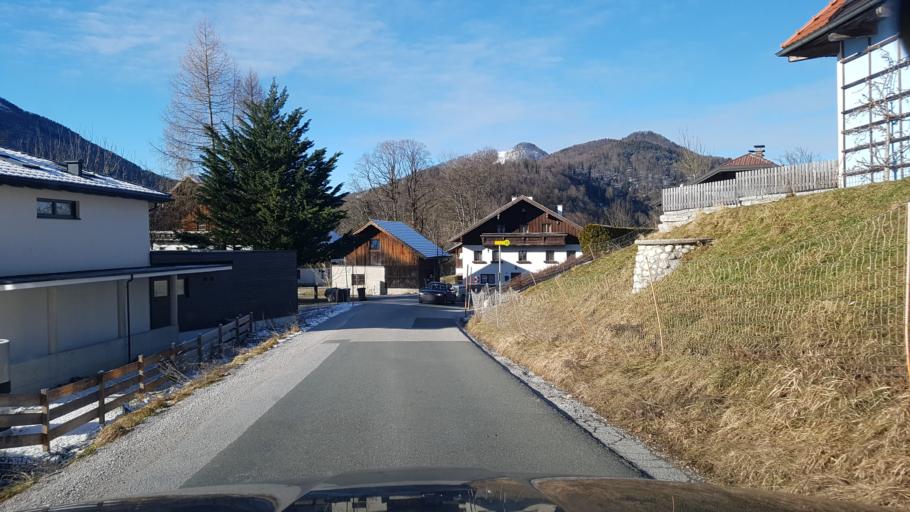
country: AT
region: Salzburg
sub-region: Politischer Bezirk Salzburg-Umgebung
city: Ebenau
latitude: 47.7712
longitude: 13.1863
